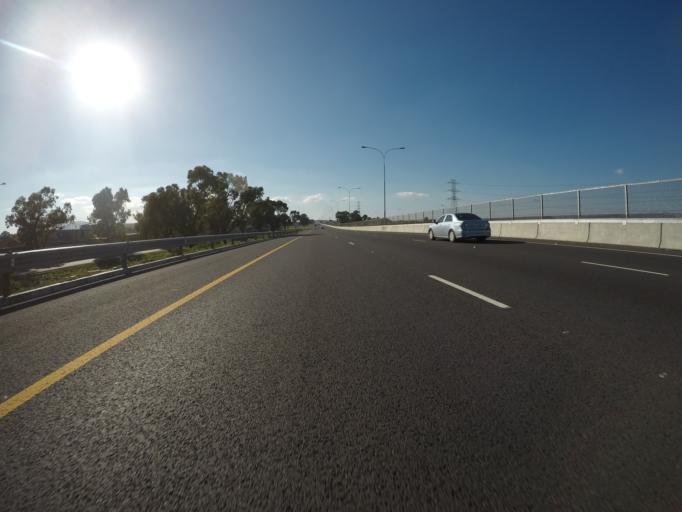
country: ZA
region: Western Cape
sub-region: City of Cape Town
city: Kraaifontein
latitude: -33.9526
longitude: 18.6576
